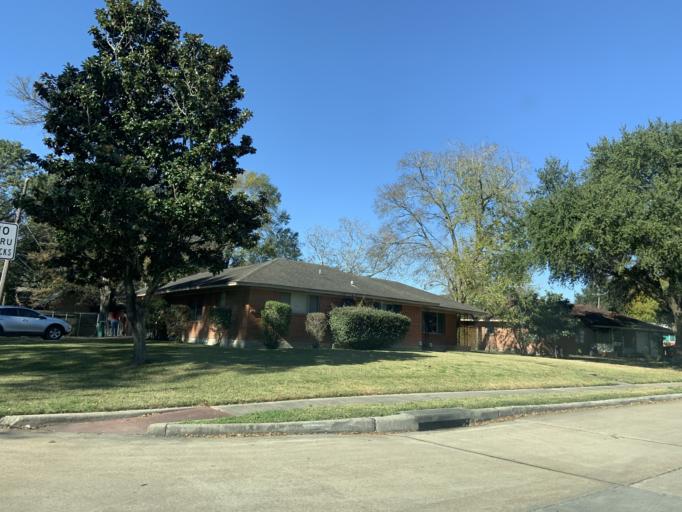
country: US
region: Texas
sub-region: Harris County
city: Bellaire
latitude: 29.6784
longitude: -95.5108
